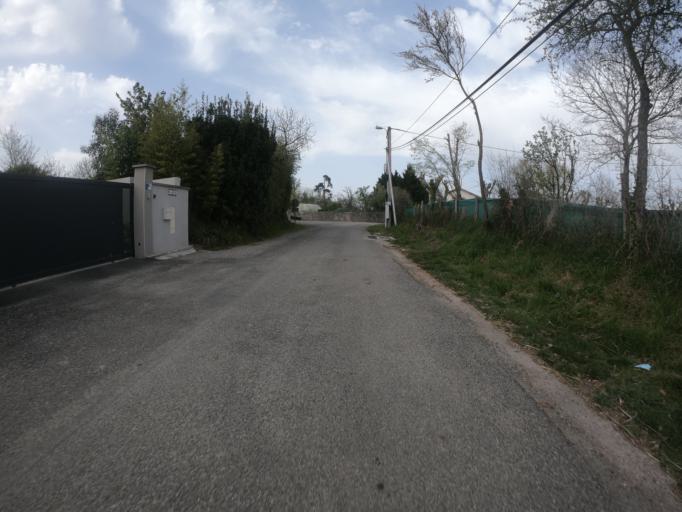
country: FR
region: Languedoc-Roussillon
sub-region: Departement de l'Aude
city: Belpech
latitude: 43.1572
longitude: 1.7201
